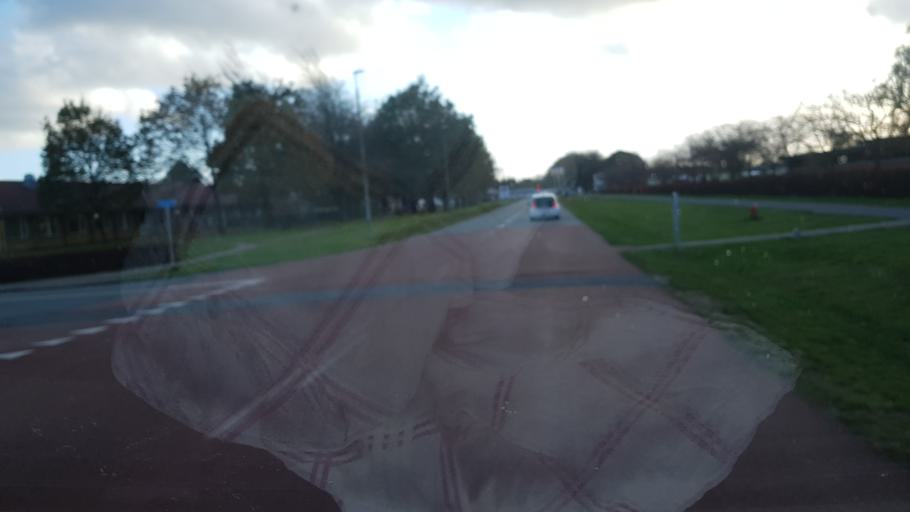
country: DK
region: South Denmark
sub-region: Billund Kommune
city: Grindsted
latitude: 55.7632
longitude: 8.9157
